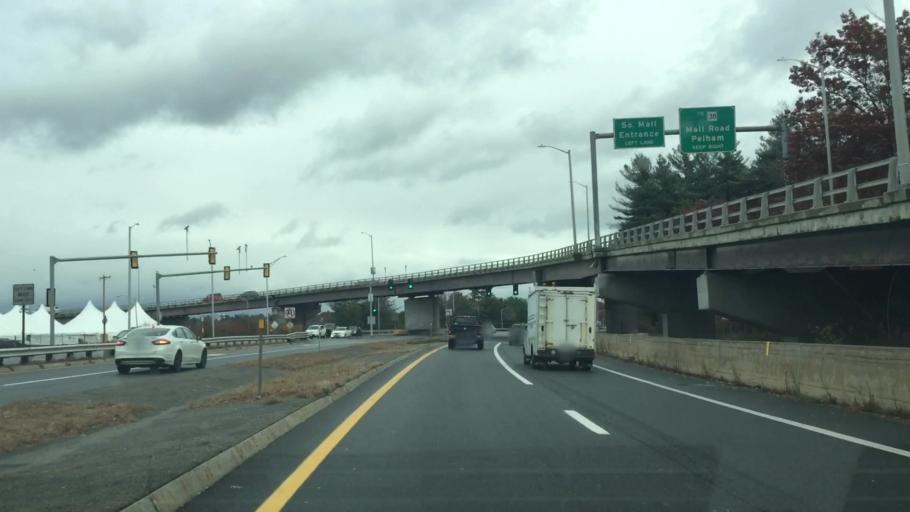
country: US
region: New Hampshire
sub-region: Rockingham County
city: Salem
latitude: 42.7657
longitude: -71.2281
